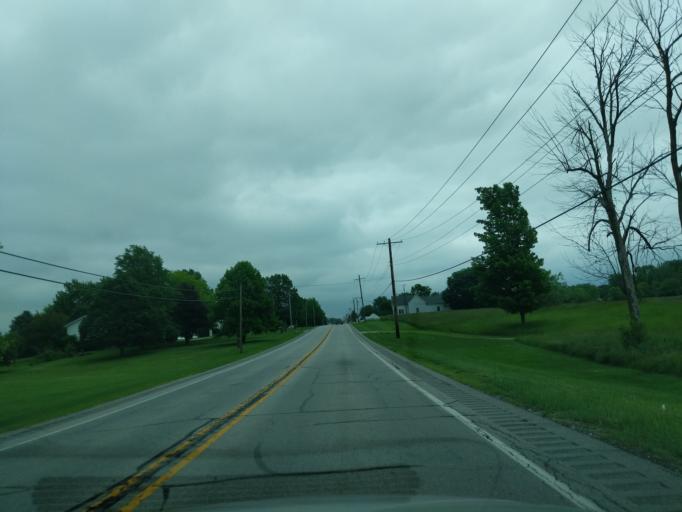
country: US
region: Indiana
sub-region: Madison County
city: Alexandria
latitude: 40.2775
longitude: -85.6810
